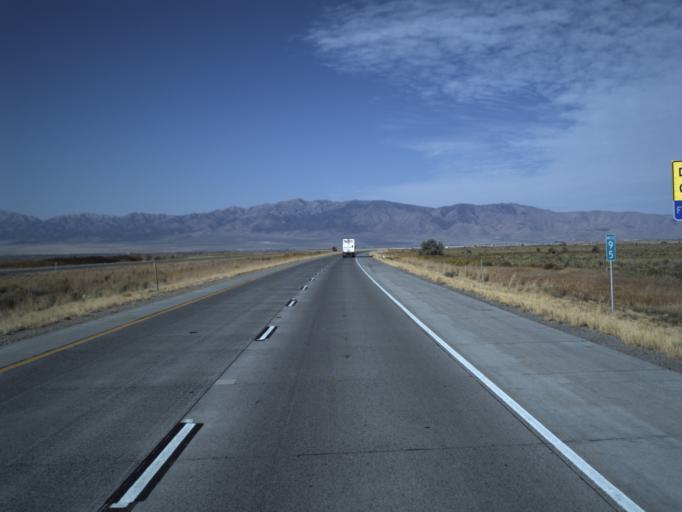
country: US
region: Utah
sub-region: Tooele County
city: Stansbury park
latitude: 40.6644
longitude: -112.3191
